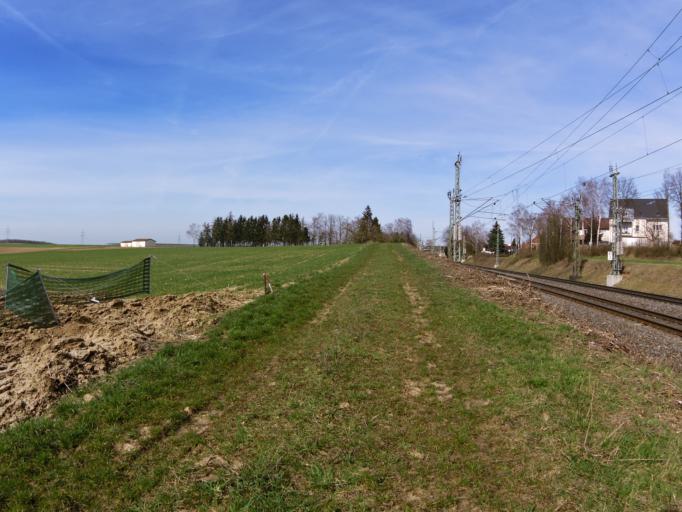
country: DE
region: Bavaria
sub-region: Regierungsbezirk Unterfranken
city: Biebelried
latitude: 49.7932
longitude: 10.0841
